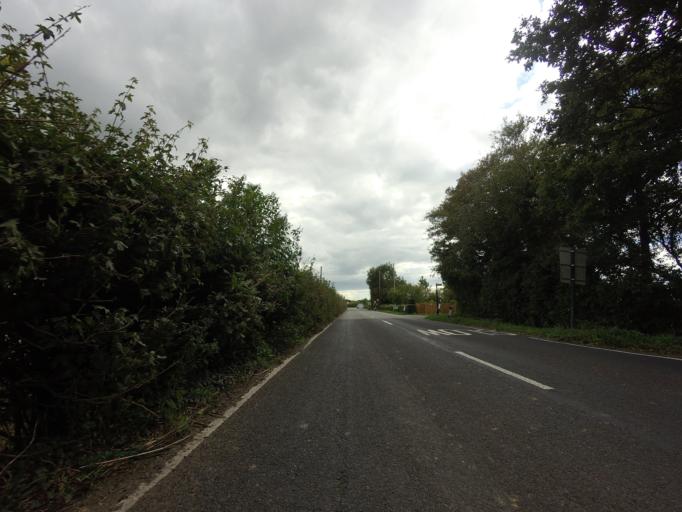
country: GB
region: England
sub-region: Kent
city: Marden
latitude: 51.1663
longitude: 0.4495
